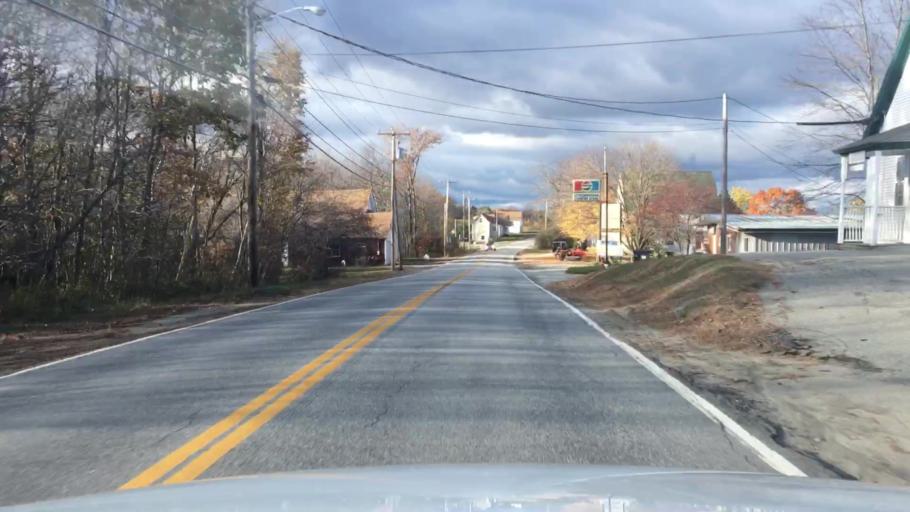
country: US
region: Maine
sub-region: Androscoggin County
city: Leeds
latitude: 44.3016
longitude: -70.1181
